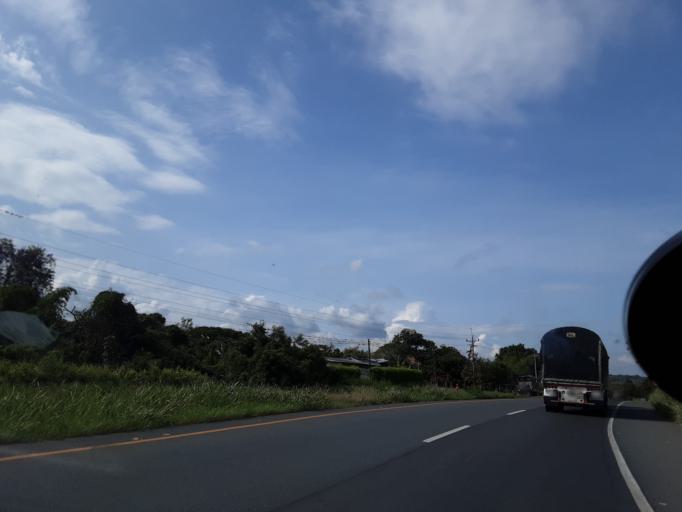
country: CO
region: Valle del Cauca
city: Buga
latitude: 3.8447
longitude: -76.2992
